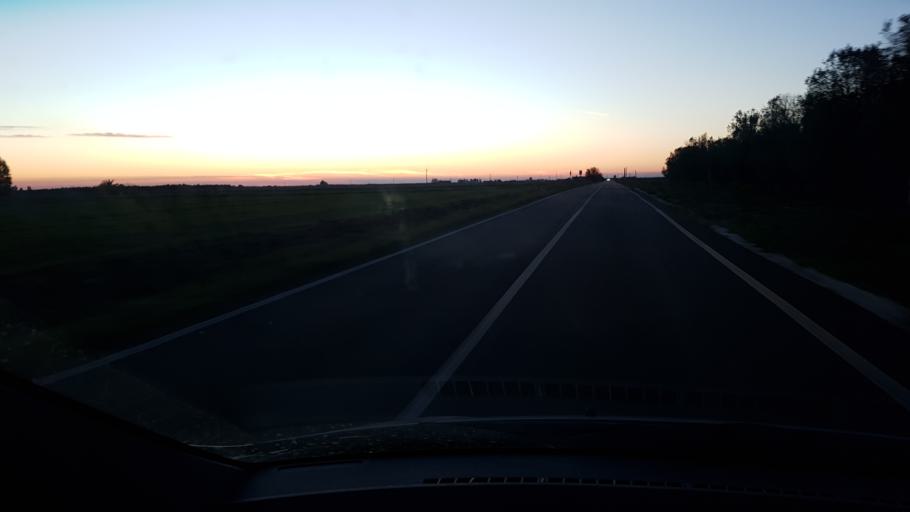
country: IT
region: Apulia
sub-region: Provincia di Brindisi
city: Tuturano
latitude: 40.5279
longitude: 17.9068
